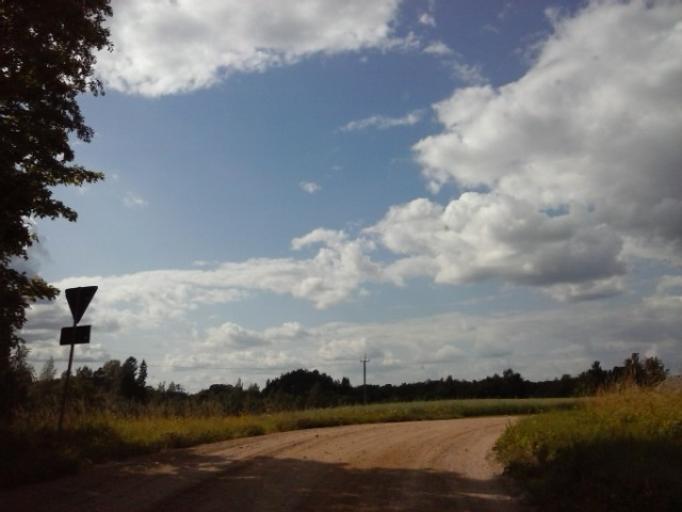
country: EE
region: Vorumaa
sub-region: Voru linn
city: Voru
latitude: 57.7506
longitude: 27.1382
